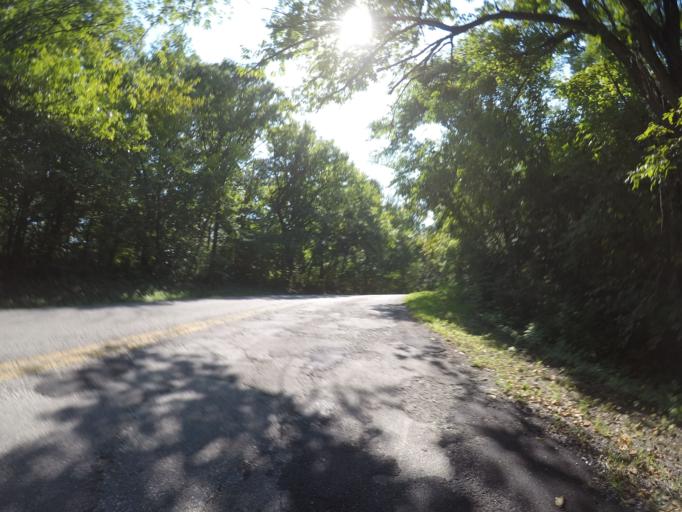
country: US
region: Missouri
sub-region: Platte County
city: Parkville
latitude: 39.1629
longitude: -94.7663
